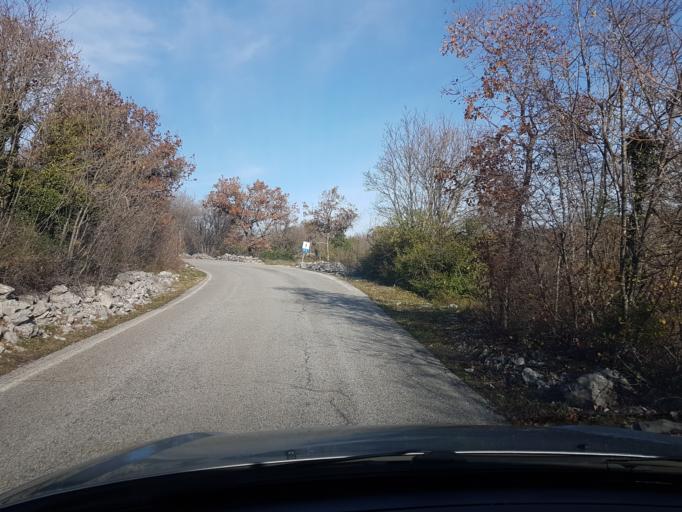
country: IT
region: Friuli Venezia Giulia
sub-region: Provincia di Trieste
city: Sistiana-Visogliano
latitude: 45.7810
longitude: 13.6404
